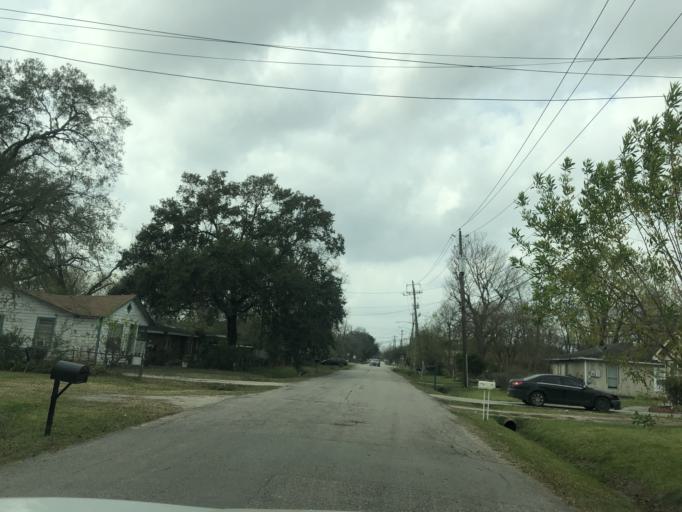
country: US
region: Texas
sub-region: Harris County
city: Jacinto City
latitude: 29.8062
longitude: -95.2827
